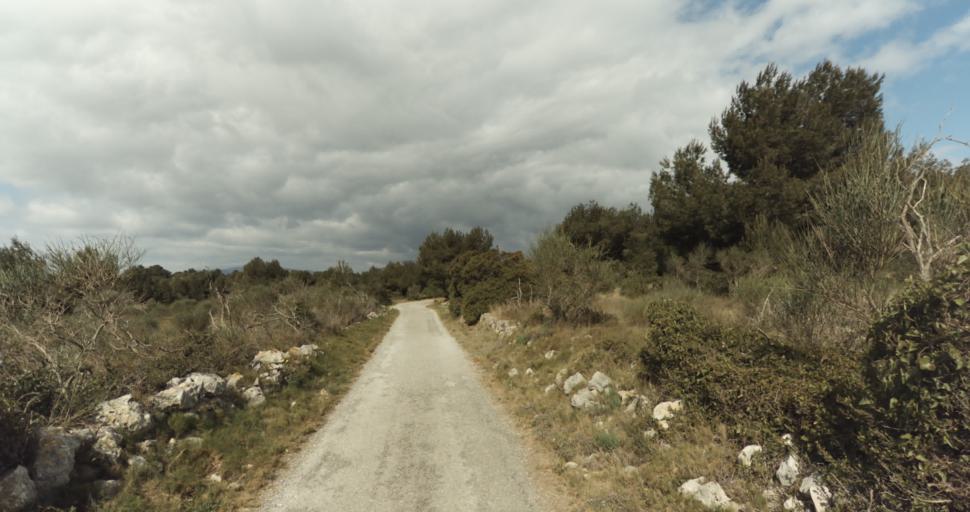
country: FR
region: Languedoc-Roussillon
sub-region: Departement de l'Aude
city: Leucate
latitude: 42.9187
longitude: 3.0503
